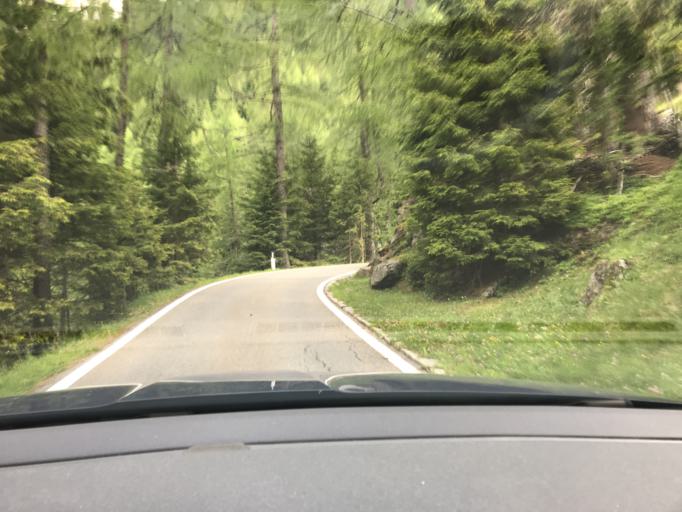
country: IT
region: Trentino-Alto Adige
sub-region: Bolzano
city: San Martino
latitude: 46.8894
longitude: 12.1928
